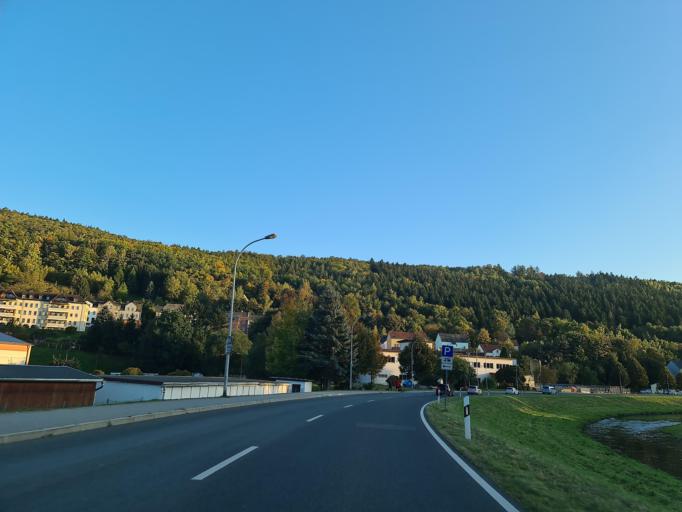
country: DE
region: Saxony
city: Elsterberg
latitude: 50.6101
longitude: 12.1748
